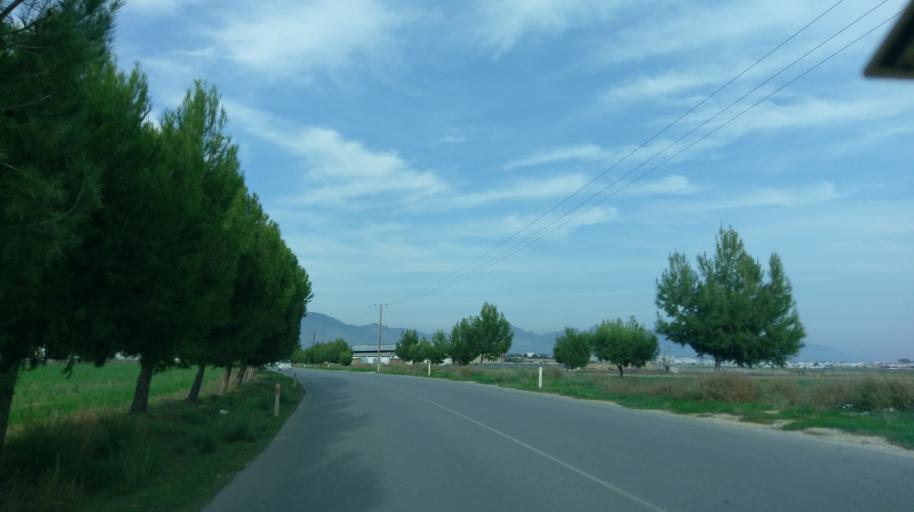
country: CY
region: Lefkosia
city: Mammari
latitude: 35.2069
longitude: 33.2756
